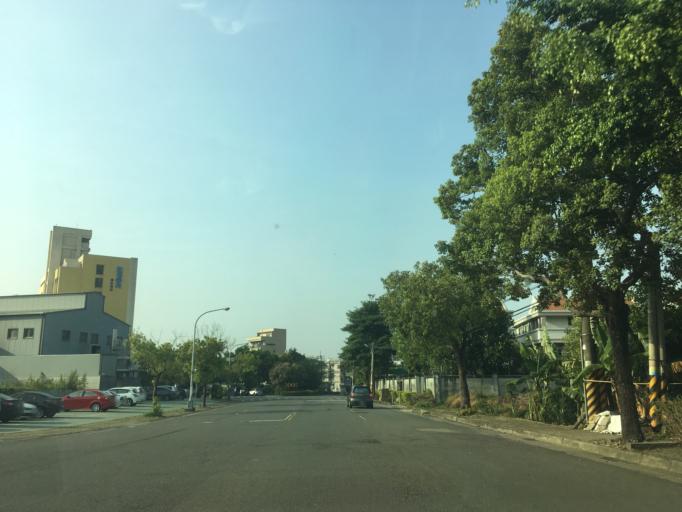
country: TW
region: Taiwan
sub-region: Taichung City
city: Taichung
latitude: 24.0602
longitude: 120.6802
